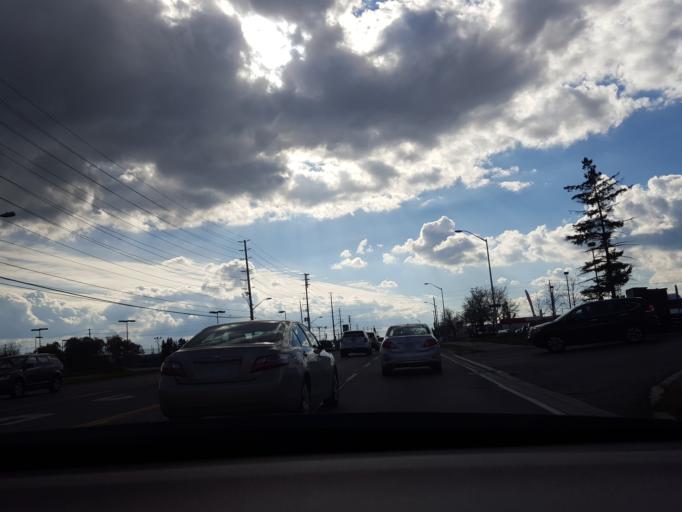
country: CA
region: Ontario
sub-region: Halton
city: Milton
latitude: 43.5082
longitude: -79.8597
